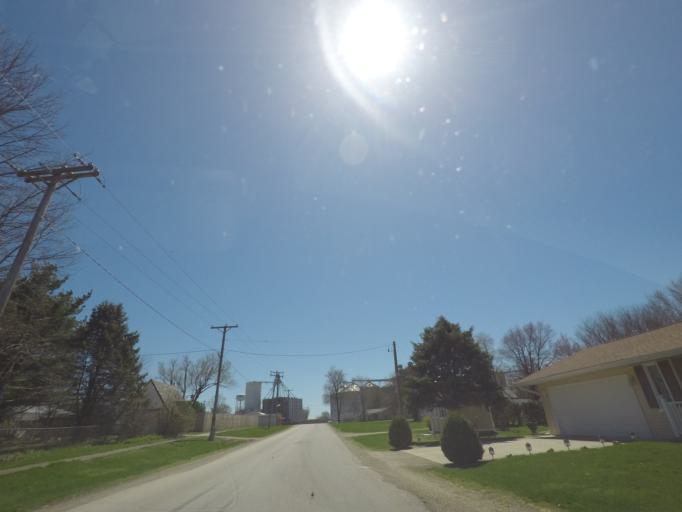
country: US
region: Illinois
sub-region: Macon County
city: Warrensburg
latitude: 39.9683
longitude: -89.1627
